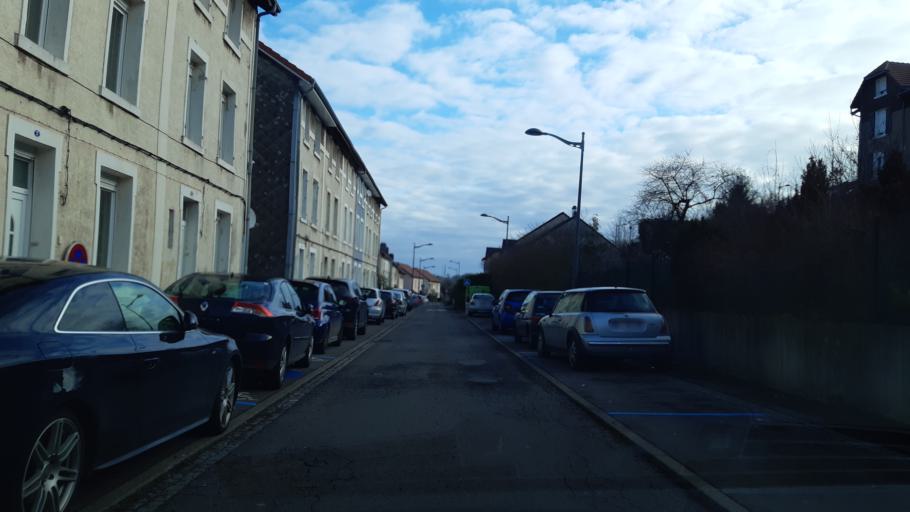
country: FR
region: Lorraine
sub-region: Departement de Meurthe-et-Moselle
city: Villerupt
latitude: 49.4712
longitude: 5.9336
